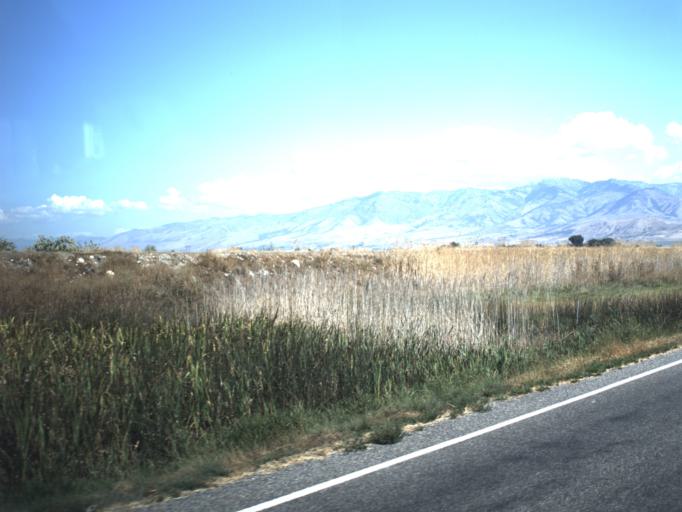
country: US
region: Utah
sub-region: Cache County
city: Benson
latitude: 41.8450
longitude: -111.9126
